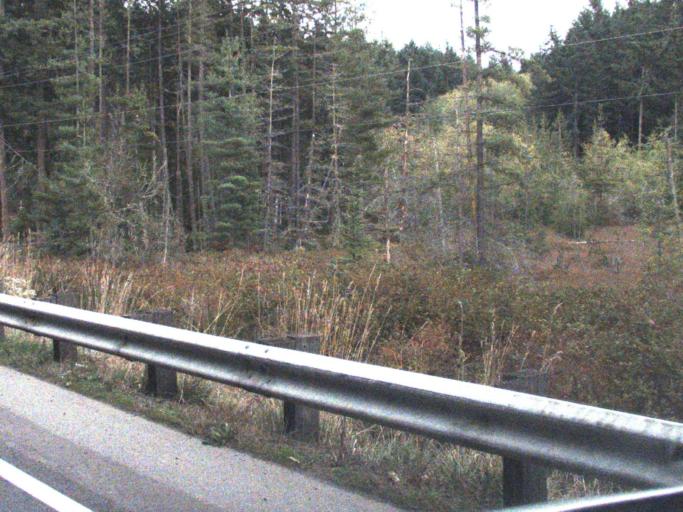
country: US
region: Washington
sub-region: Island County
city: Langley
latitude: 48.0033
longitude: -122.4429
